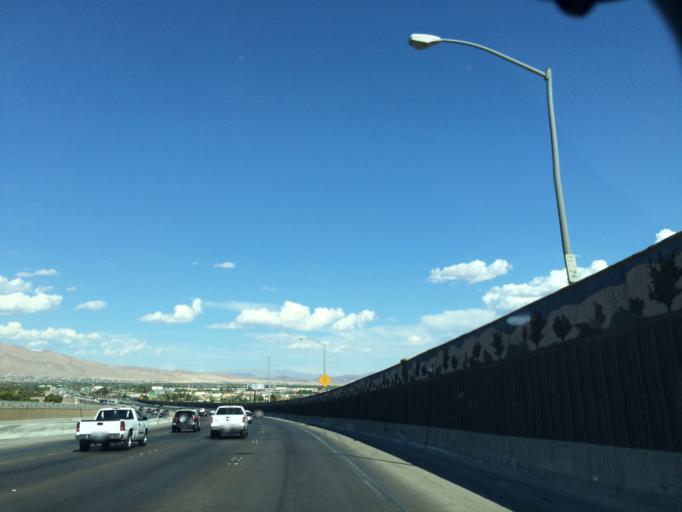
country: US
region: Nevada
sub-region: Clark County
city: Las Vegas
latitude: 36.1686
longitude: -115.1269
